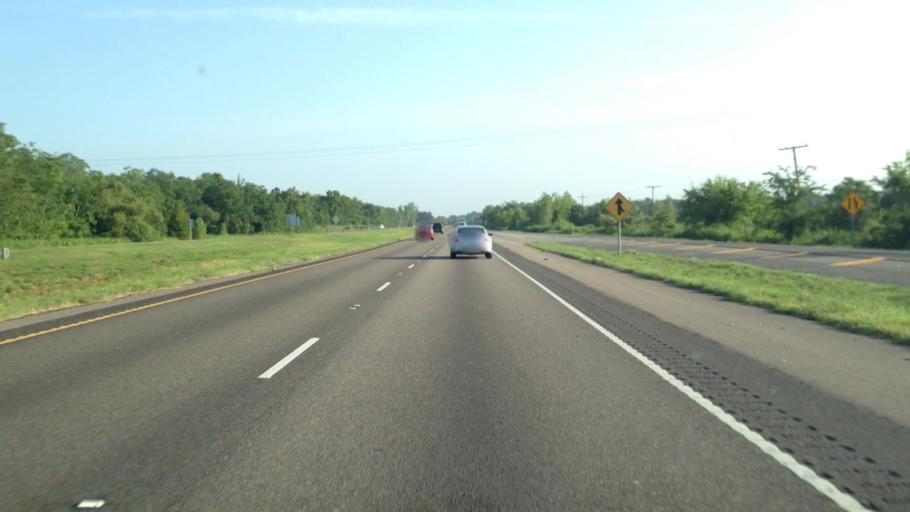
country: US
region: Louisiana
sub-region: Tangipahoa Parish
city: Ponchatoula
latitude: 30.4013
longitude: -90.4308
